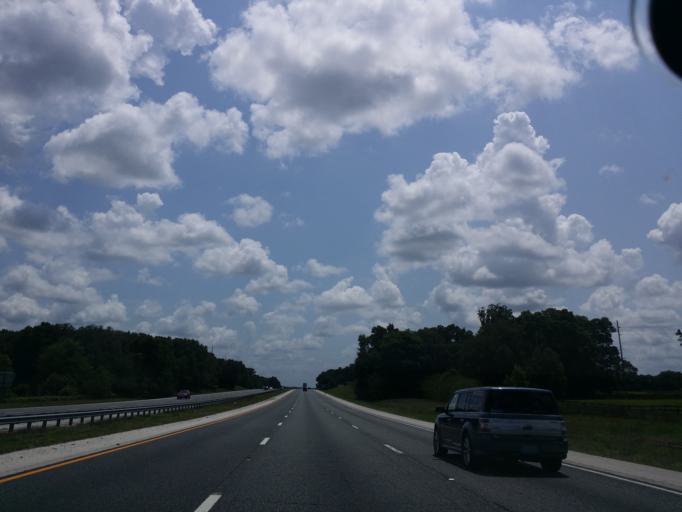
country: US
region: Florida
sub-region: Marion County
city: Ocala
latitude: 29.2833
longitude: -82.1991
